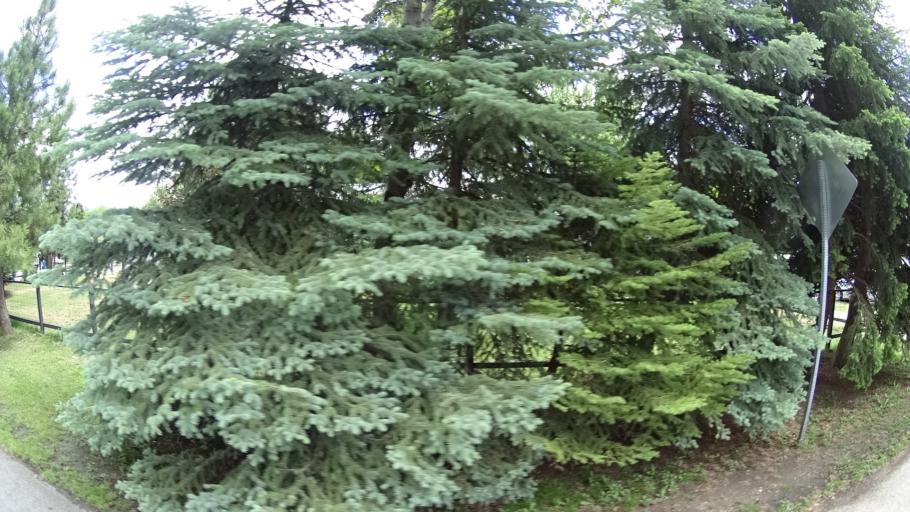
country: US
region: Idaho
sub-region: Ada County
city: Boise
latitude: 43.5864
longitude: -116.1986
